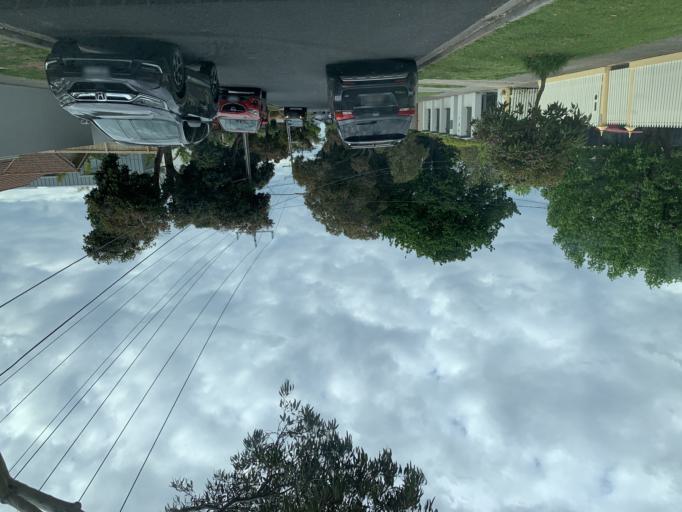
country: AU
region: Victoria
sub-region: Bayside
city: Hampton
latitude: -37.9300
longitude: 144.9998
